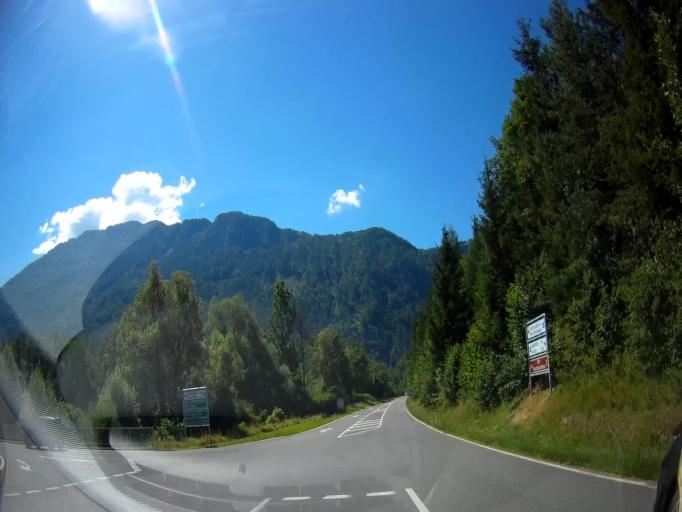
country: AT
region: Carinthia
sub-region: Politischer Bezirk Volkermarkt
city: Sittersdorf
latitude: 46.5361
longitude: 14.5899
